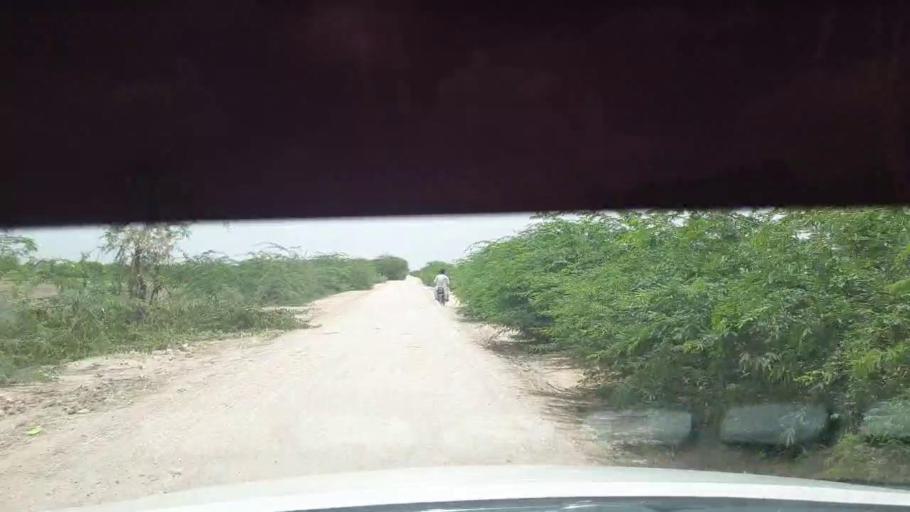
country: PK
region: Sindh
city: Kadhan
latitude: 24.4650
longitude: 69.0190
